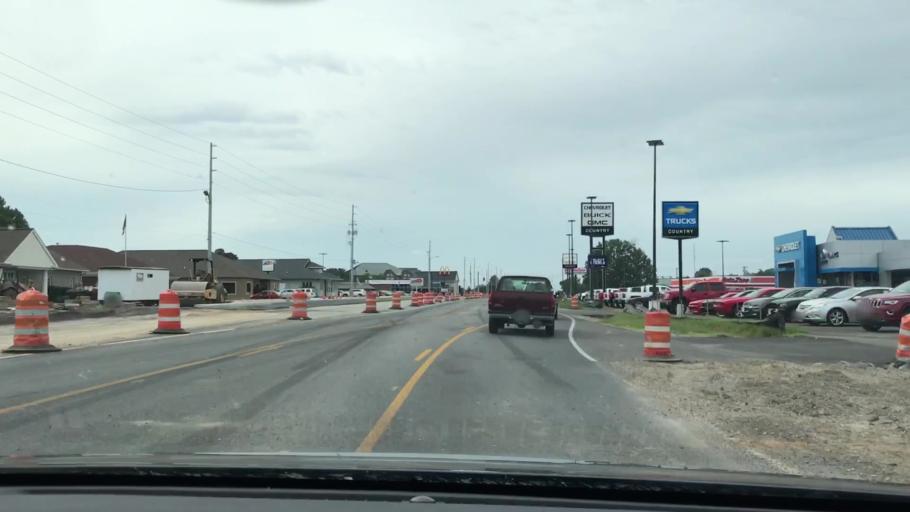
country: US
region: Kentucky
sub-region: Marshall County
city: Benton
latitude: 36.8646
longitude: -88.3526
